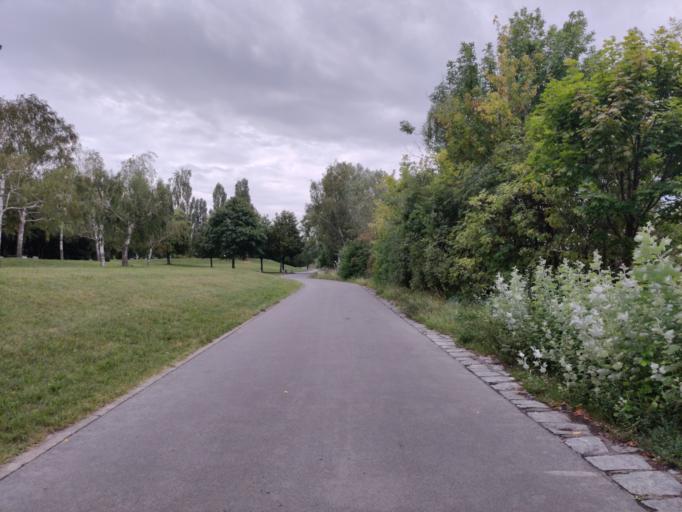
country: AT
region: Vienna
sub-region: Wien Stadt
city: Vienna
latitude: 48.2327
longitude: 16.4028
